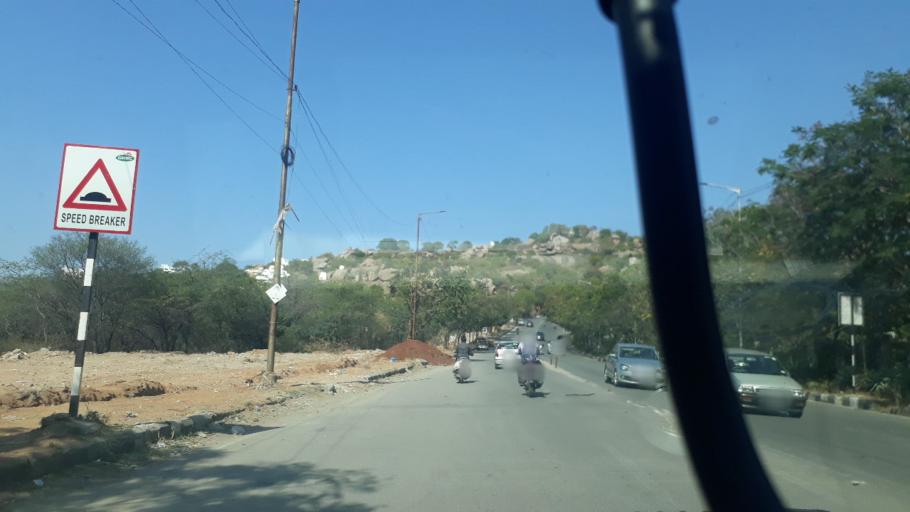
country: IN
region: Telangana
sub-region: Hyderabad
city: Hyderabad
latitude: 17.4160
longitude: 78.3943
